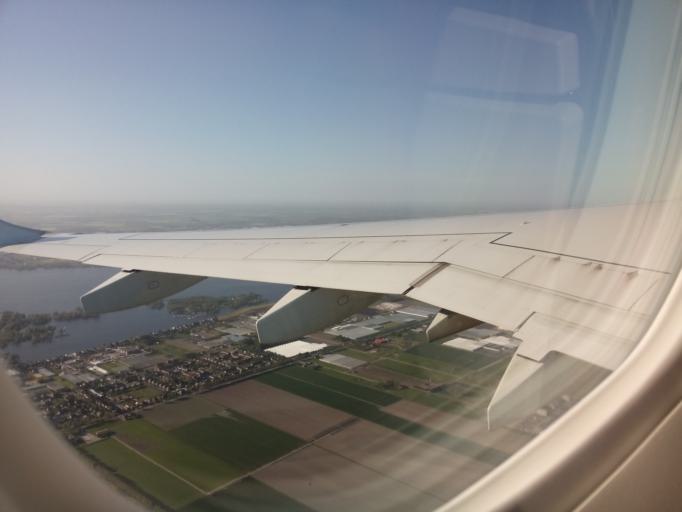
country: NL
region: North Holland
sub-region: Gemeente Haarlemmermeer
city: Hoofddorp
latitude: 52.2734
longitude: 4.6988
